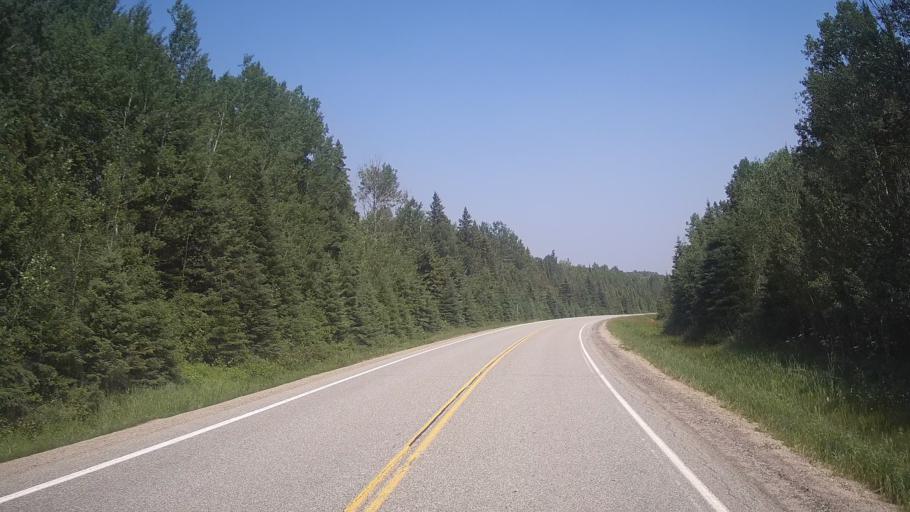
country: CA
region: Ontario
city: Timmins
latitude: 48.2324
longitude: -81.5764
